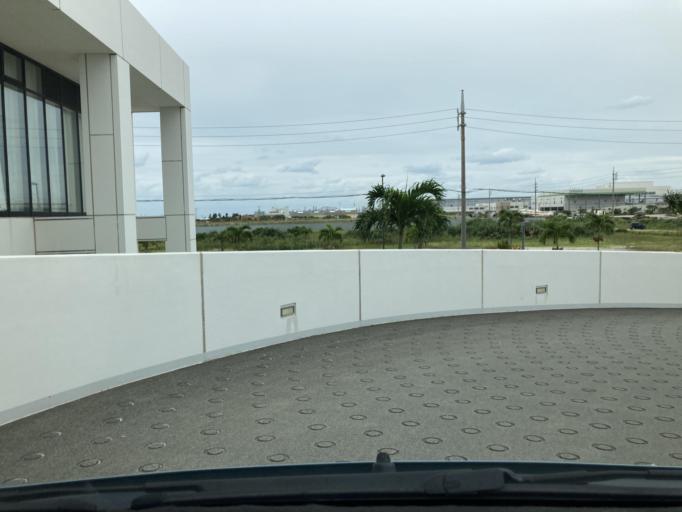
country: JP
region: Okinawa
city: Itoman
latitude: 26.1325
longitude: 127.6531
